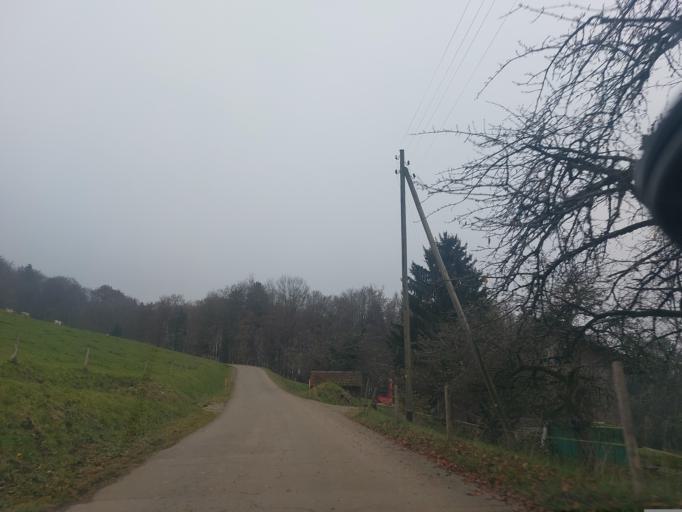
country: CH
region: Vaud
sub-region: Riviera-Pays-d'Enhaut District
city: Blonay
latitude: 46.4929
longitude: 6.8938
